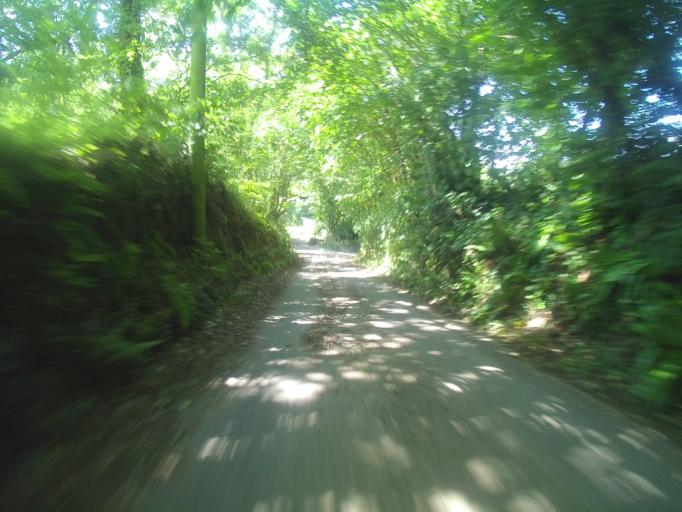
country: GB
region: England
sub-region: Devon
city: Dartmouth
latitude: 50.3672
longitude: -3.6417
